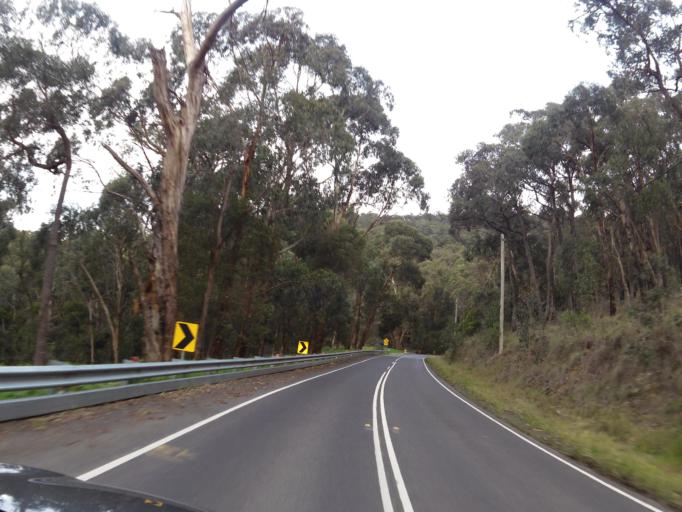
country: AU
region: Victoria
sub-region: Knox
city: The Basin
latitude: -37.8661
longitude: 145.3226
